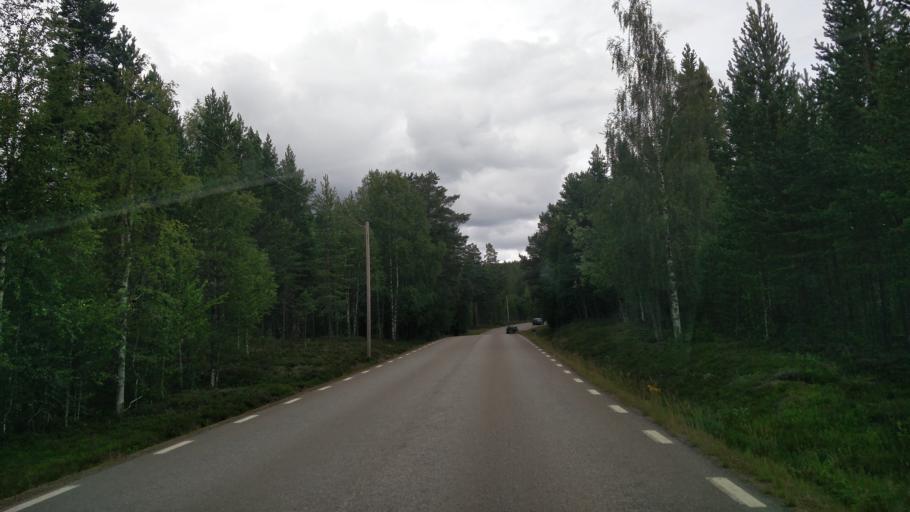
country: NO
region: Hedmark
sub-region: Trysil
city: Innbygda
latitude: 61.1742
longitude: 12.8479
